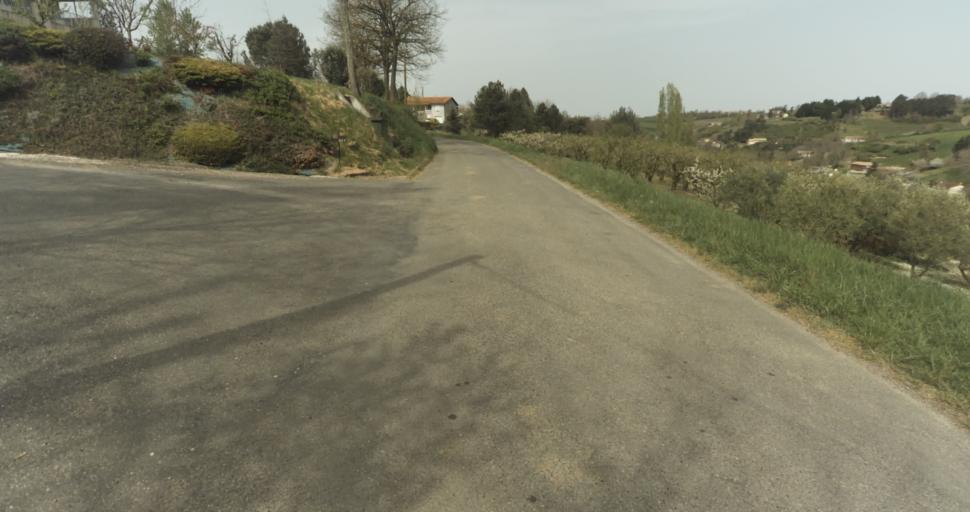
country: FR
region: Midi-Pyrenees
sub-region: Departement du Tarn-et-Garonne
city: Moissac
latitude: 44.1031
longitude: 1.0679
